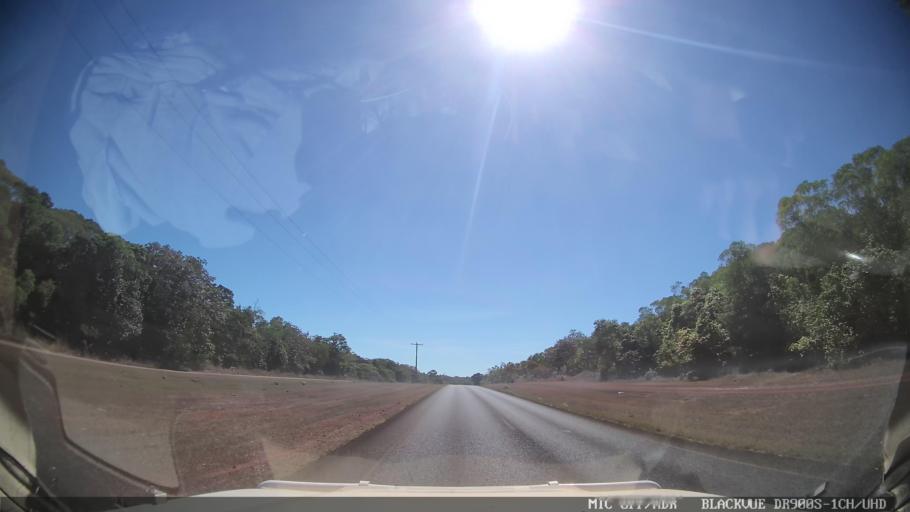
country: AU
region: Queensland
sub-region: Torres
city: Thursday Island
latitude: -10.9014
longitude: 142.3343
